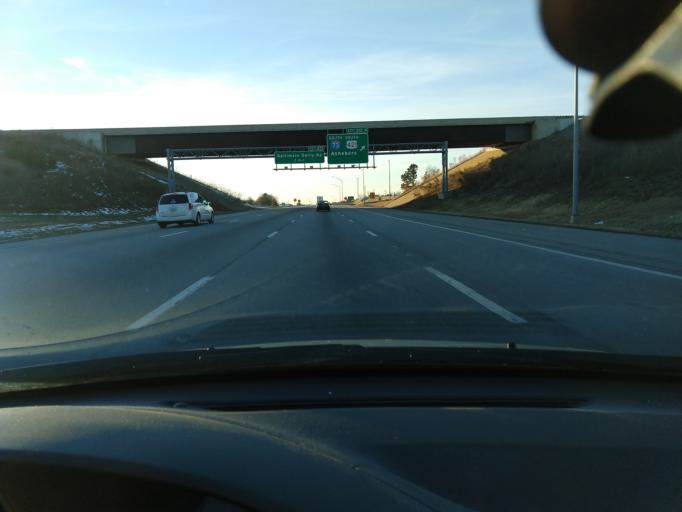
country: US
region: North Carolina
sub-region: Guilford County
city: Jamestown
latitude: 36.0670
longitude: -79.9193
